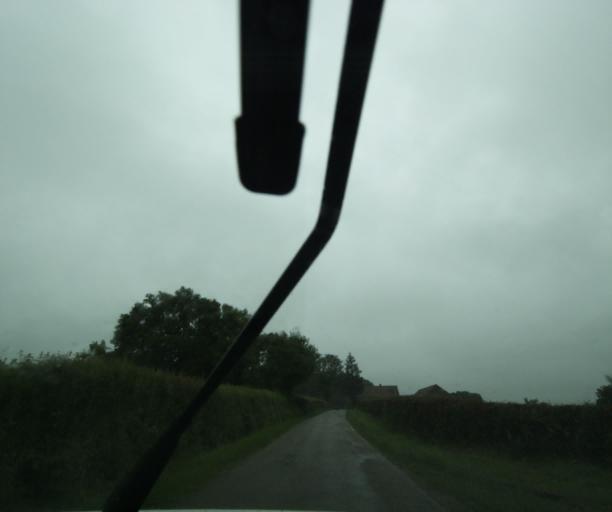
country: FR
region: Bourgogne
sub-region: Departement de Saone-et-Loire
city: Charolles
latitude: 46.4066
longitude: 4.2459
